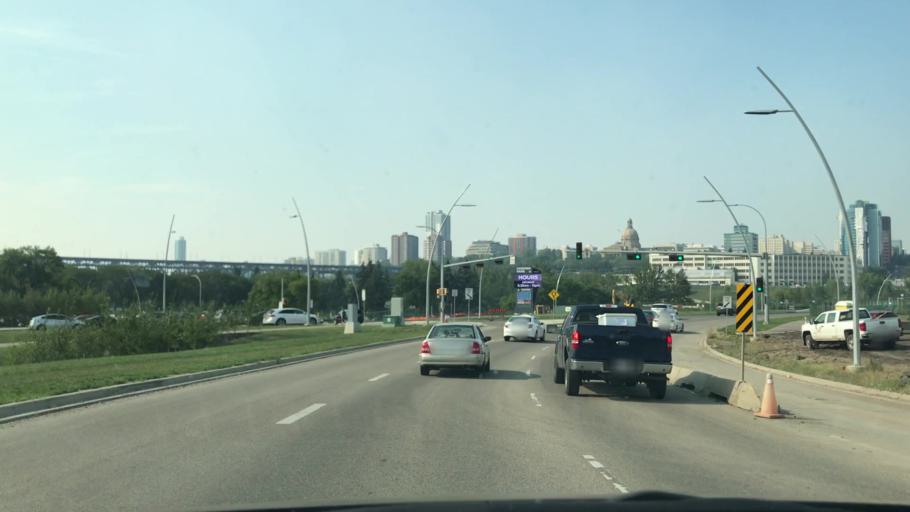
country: CA
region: Alberta
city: Edmonton
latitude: 53.5256
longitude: -113.5023
